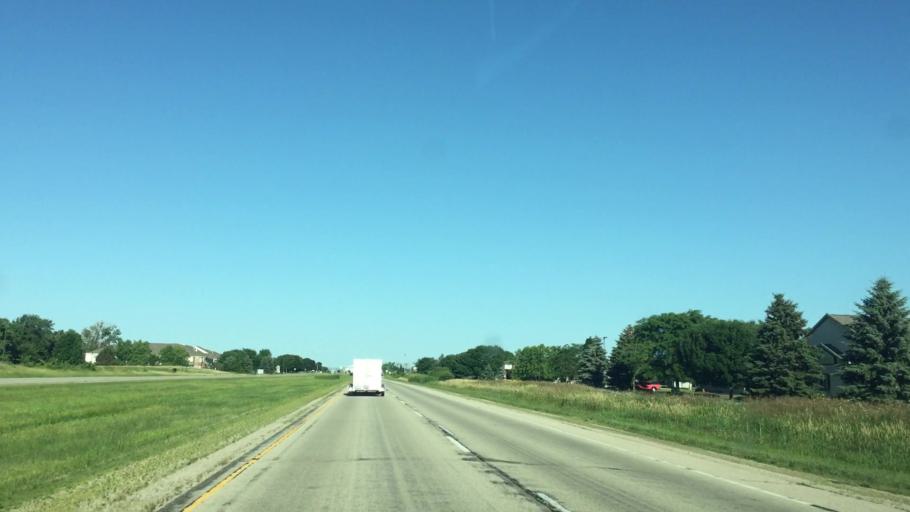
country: US
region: Wisconsin
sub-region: Winnebago County
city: Menasha
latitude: 44.2623
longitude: -88.4904
